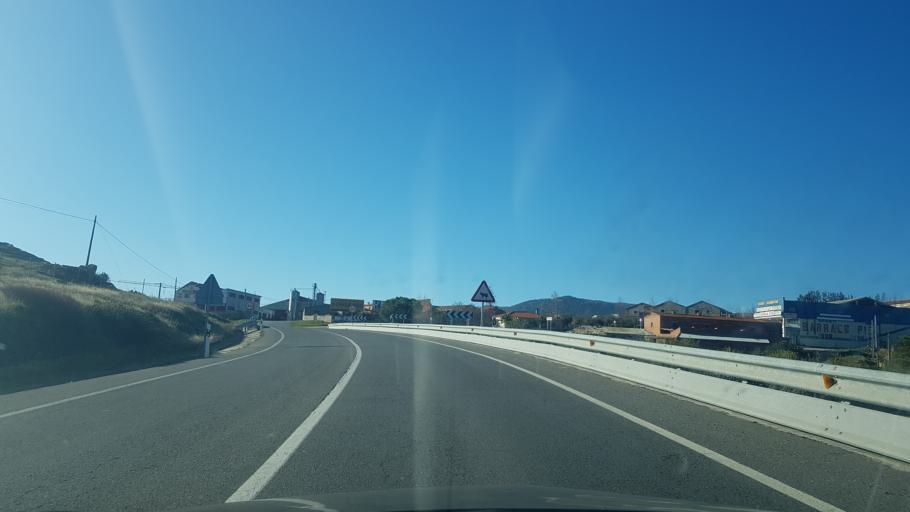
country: ES
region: Castille and Leon
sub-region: Provincia de Avila
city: Barraco
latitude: 40.4726
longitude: -4.6342
